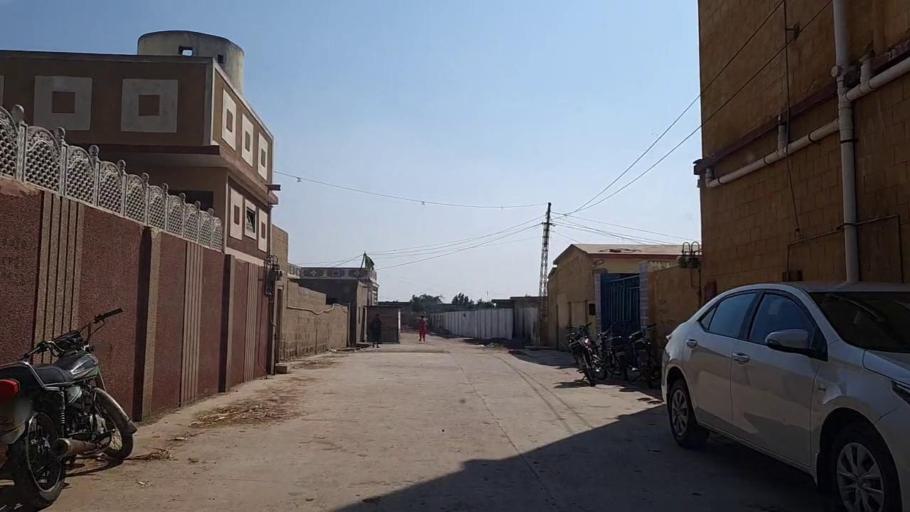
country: PK
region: Sindh
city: Thatta
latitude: 24.7945
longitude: 67.9602
